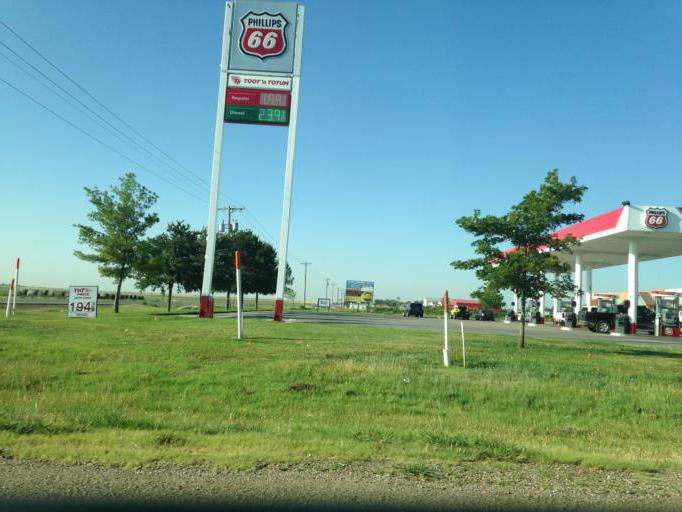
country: US
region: Texas
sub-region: Randall County
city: Canyon
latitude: 35.1171
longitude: -101.9383
